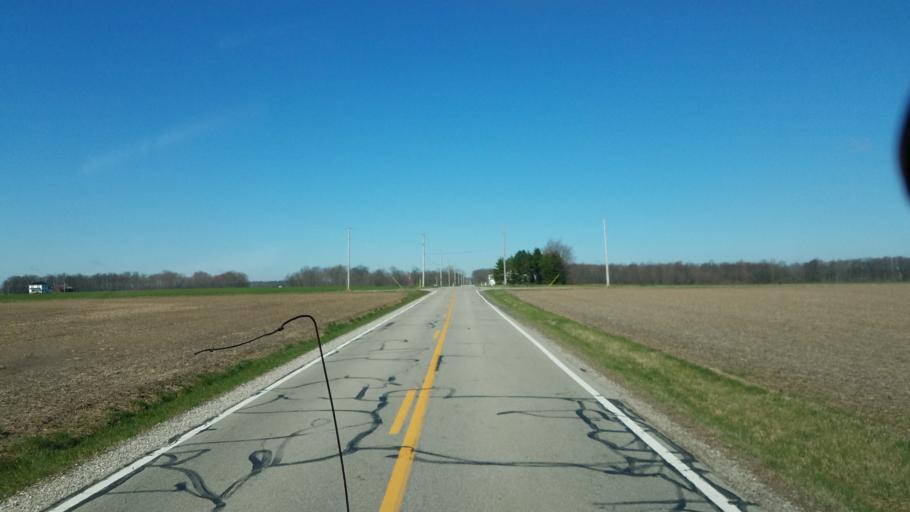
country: US
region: Ohio
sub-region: Huron County
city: Willard
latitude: 40.9820
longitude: -82.8338
